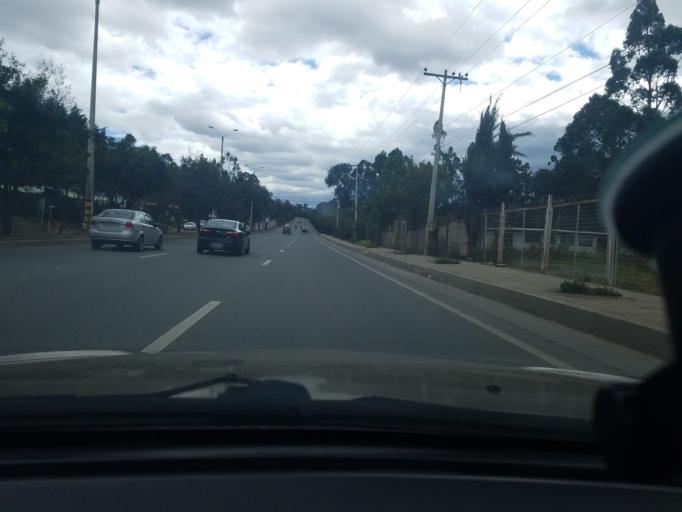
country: EC
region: Azuay
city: Llacao
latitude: -2.8545
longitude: -78.9170
